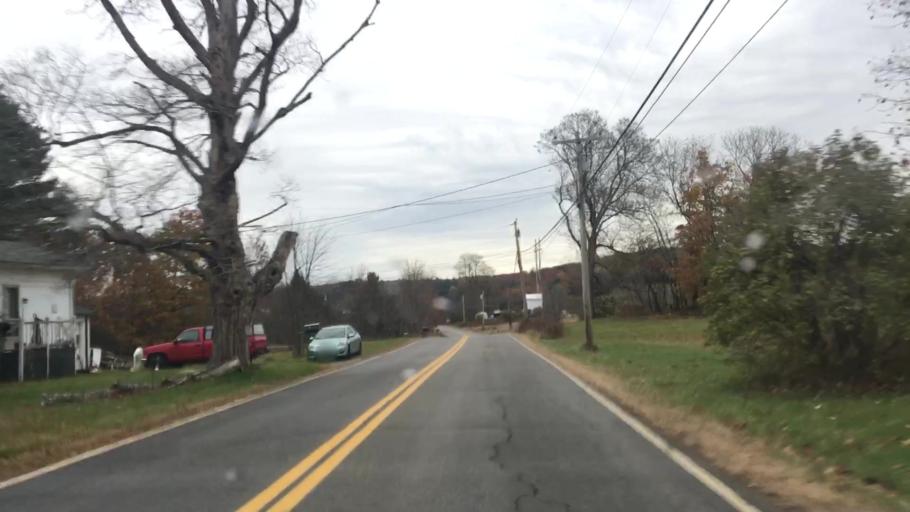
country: US
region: Maine
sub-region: Lincoln County
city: Whitefield
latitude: 44.1684
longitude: -69.6388
